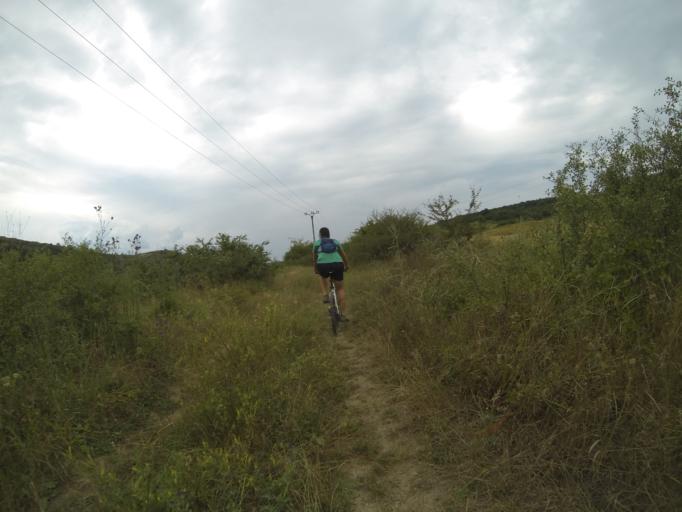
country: RO
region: Dolj
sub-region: Comuna Cotofenii din Fata
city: Cotofenii din Fata
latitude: 44.4799
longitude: 23.6884
